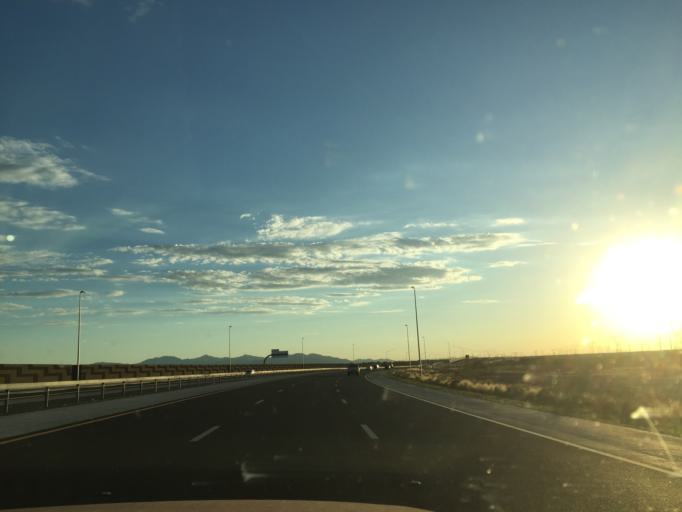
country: US
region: Arizona
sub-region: Maricopa County
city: Sun City West
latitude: 33.6992
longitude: -112.3209
